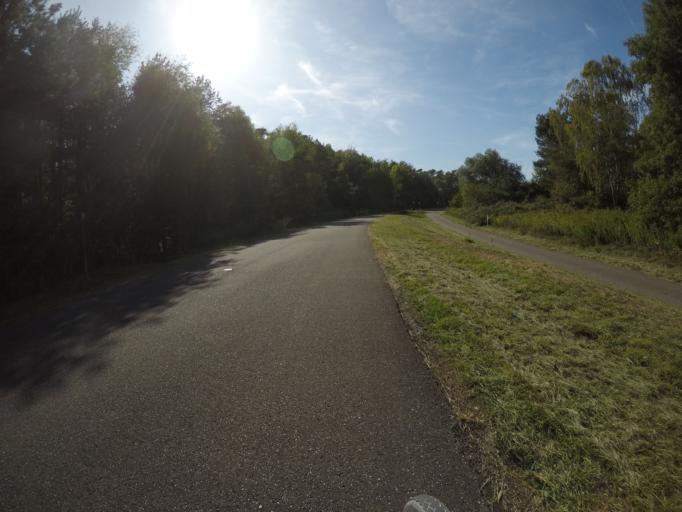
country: DE
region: Baden-Wuerttemberg
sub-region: Karlsruhe Region
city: Kronau
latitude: 49.2348
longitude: 8.6132
